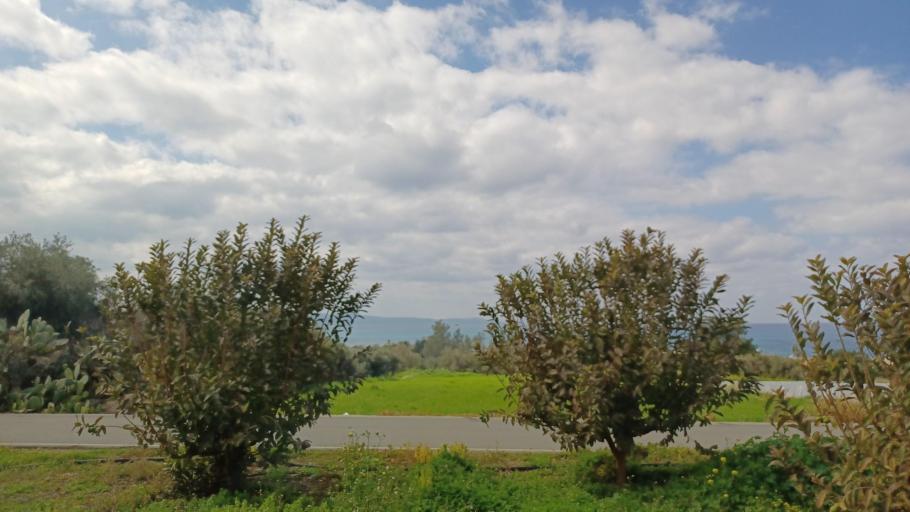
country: CY
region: Pafos
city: Polis
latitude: 35.1107
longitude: 32.5145
